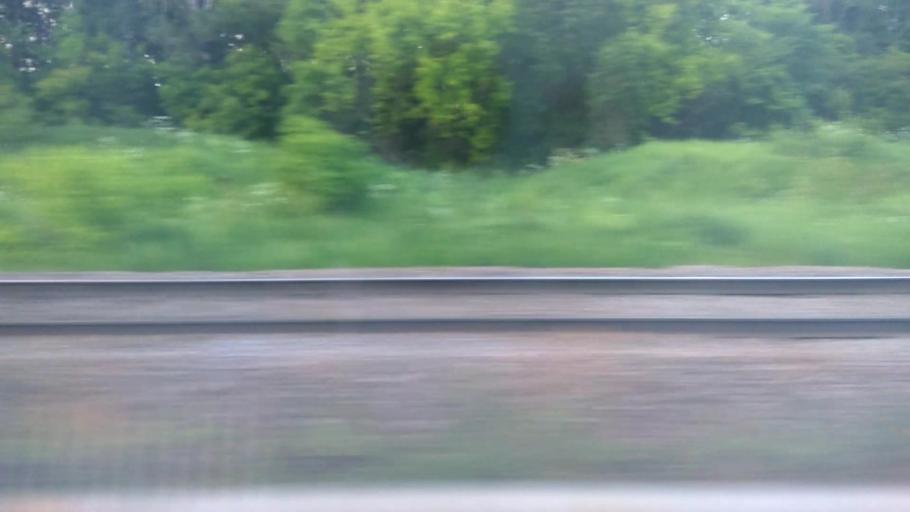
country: RU
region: Moskovskaya
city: Vostryakovo
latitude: 55.3807
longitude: 37.8159
